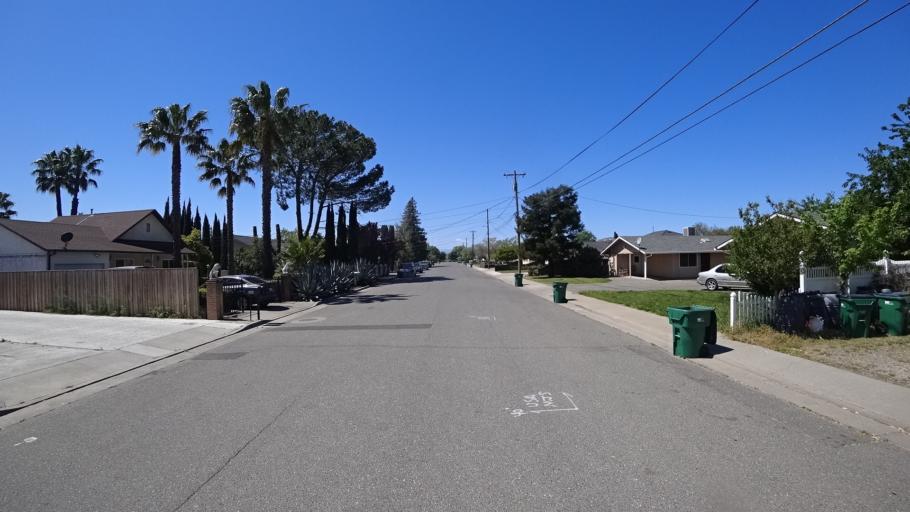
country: US
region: California
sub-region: Glenn County
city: Orland
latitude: 39.7455
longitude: -122.1790
